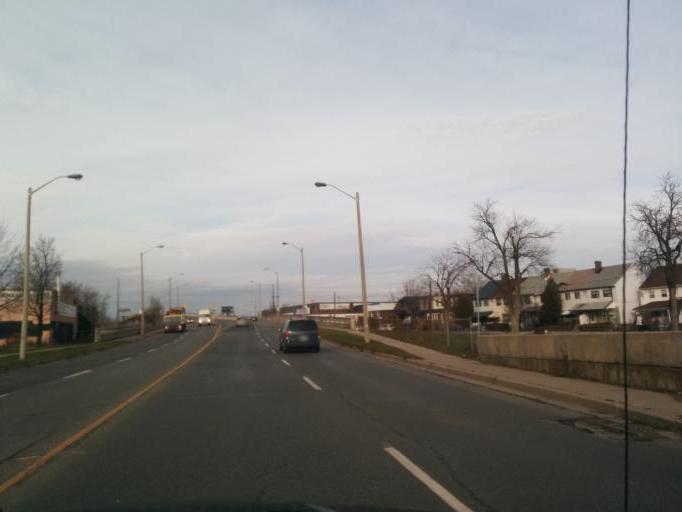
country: CA
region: Ontario
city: Etobicoke
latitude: 43.6050
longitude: -79.5066
